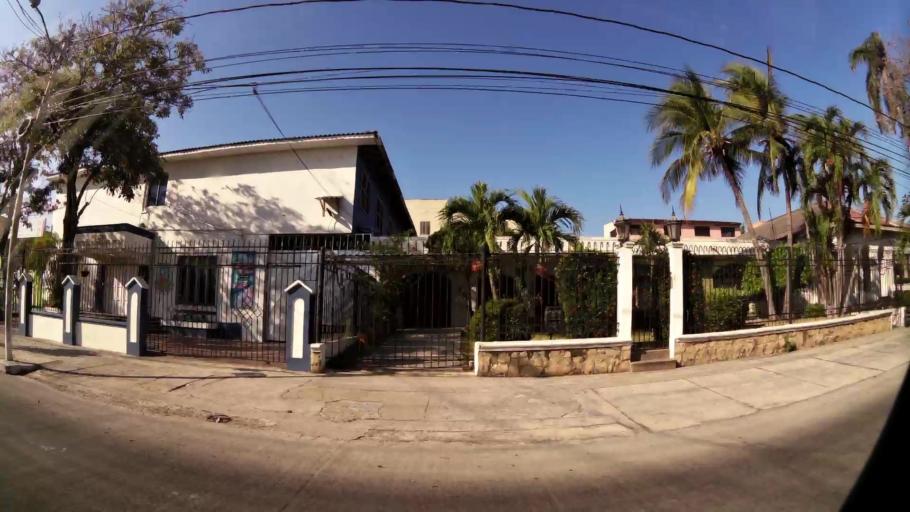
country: CO
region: Atlantico
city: Barranquilla
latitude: 11.0015
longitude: -74.7962
